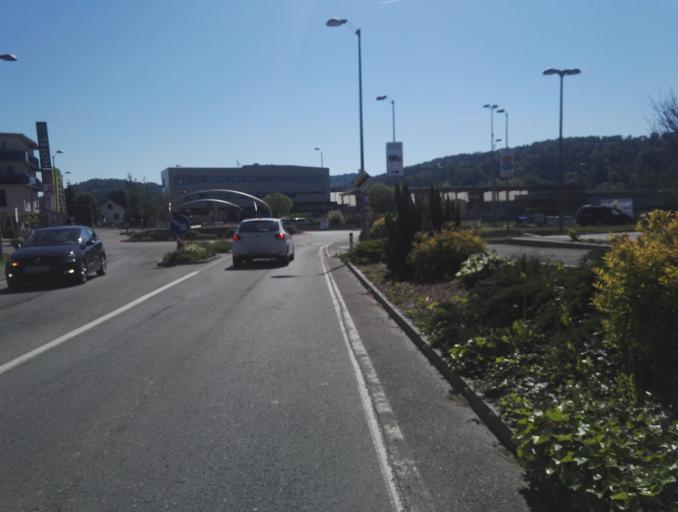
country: AT
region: Styria
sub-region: Politischer Bezirk Graz-Umgebung
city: Hart bei Graz
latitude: 47.0448
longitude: 15.5190
